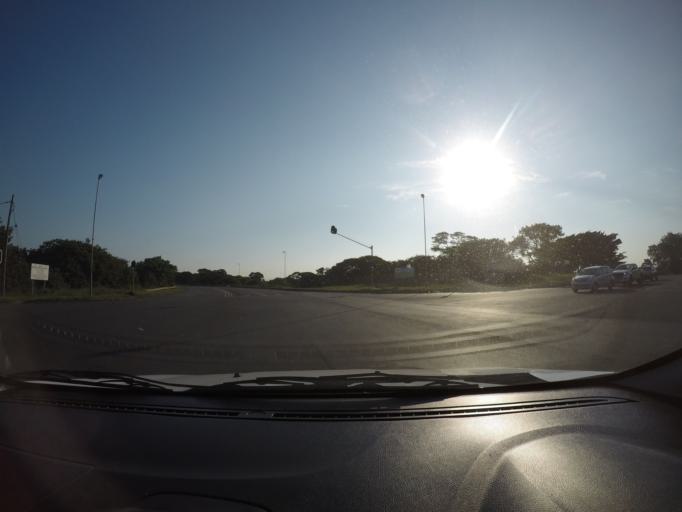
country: ZA
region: KwaZulu-Natal
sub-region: uThungulu District Municipality
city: Richards Bay
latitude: -28.7680
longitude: 32.0150
